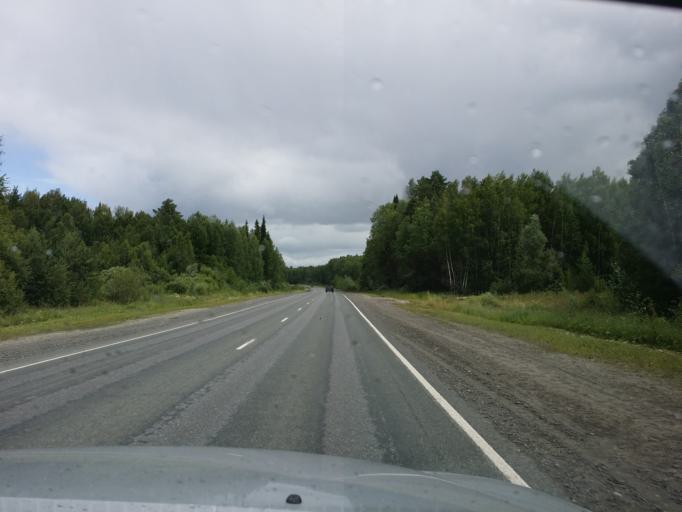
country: RU
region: Tjumen
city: Abalak
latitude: 58.4797
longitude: 68.6234
